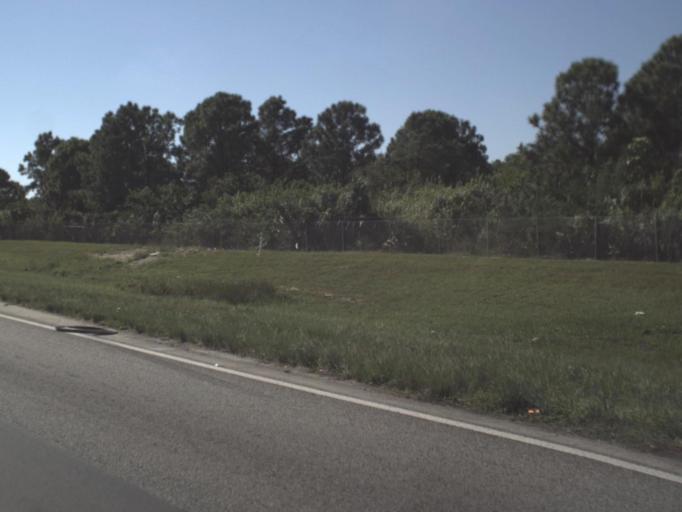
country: US
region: Florida
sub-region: Miami-Dade County
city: South Miami Heights
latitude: 25.5922
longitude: -80.3698
